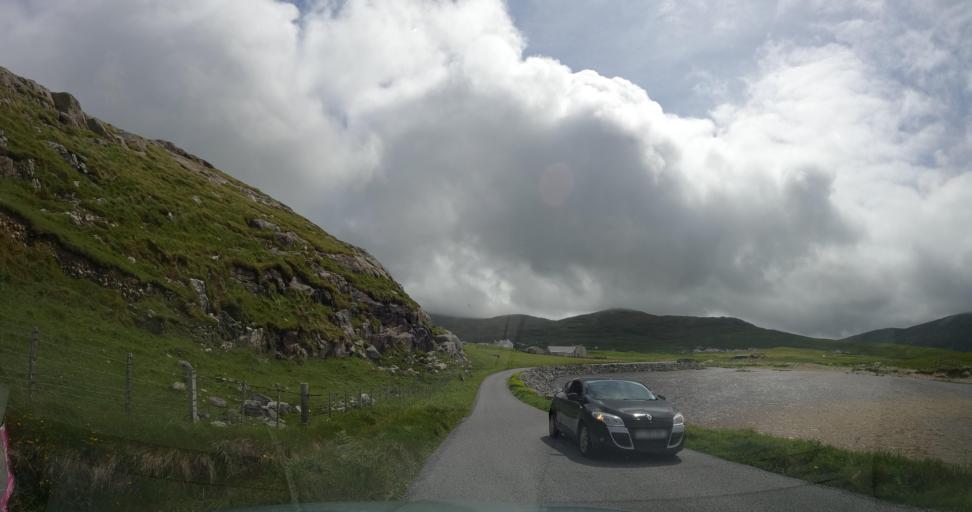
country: GB
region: Scotland
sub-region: Eilean Siar
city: Barra
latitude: 56.9889
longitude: -7.5090
